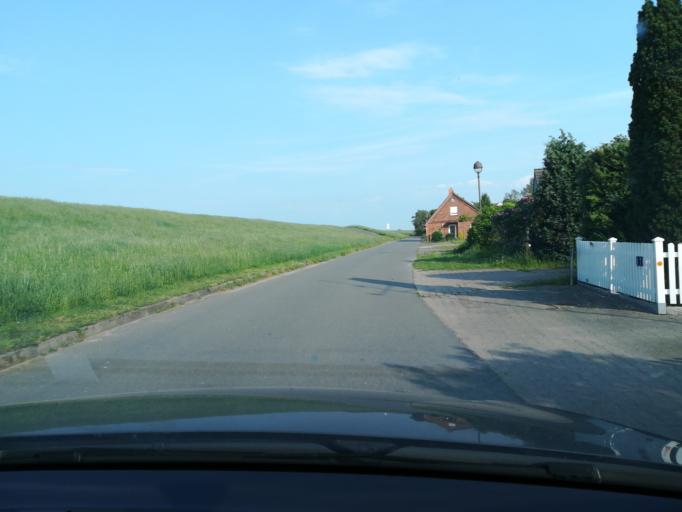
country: DE
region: Lower Saxony
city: Artlenburg
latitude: 53.3848
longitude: 10.4638
